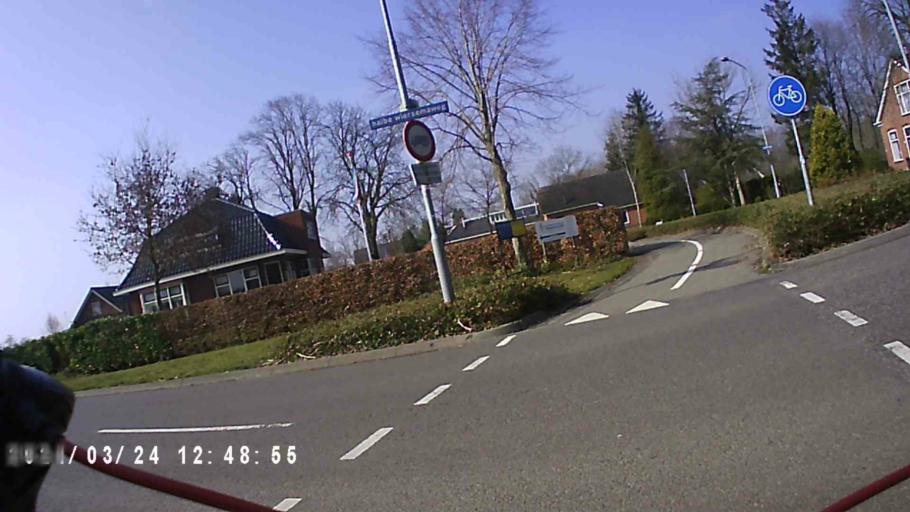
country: NL
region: Groningen
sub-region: Gemeente Leek
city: Leek
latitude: 53.1657
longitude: 6.3344
